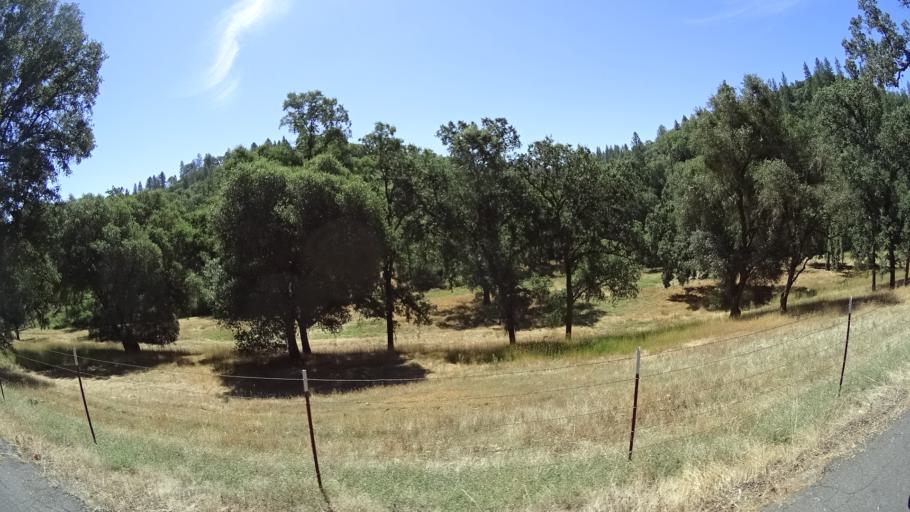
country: US
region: California
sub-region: Calaveras County
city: Angels Camp
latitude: 38.1377
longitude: -120.5559
